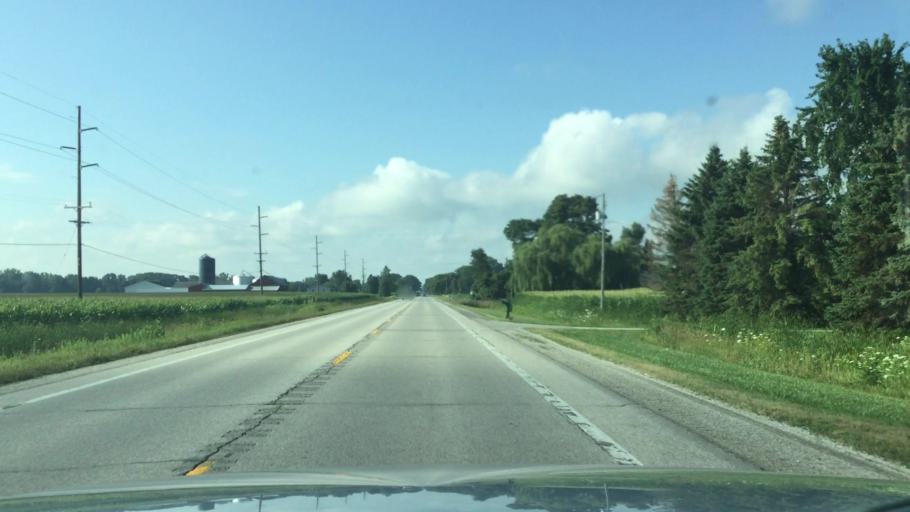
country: US
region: Michigan
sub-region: Saginaw County
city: Frankenmuth
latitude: 43.2768
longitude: -83.7358
